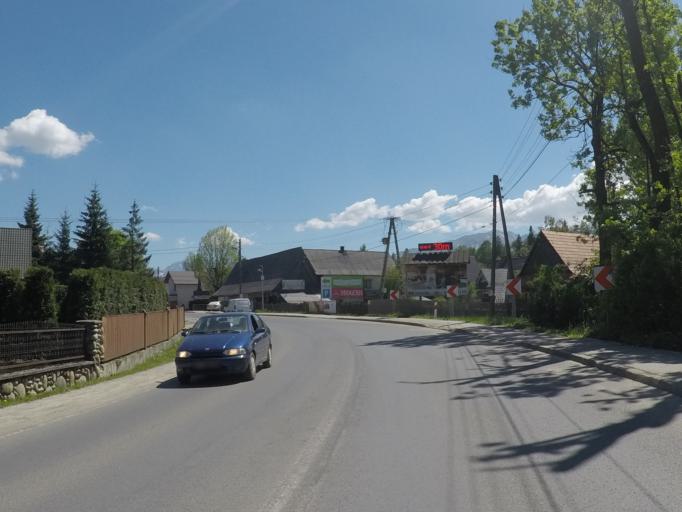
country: PL
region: Lesser Poland Voivodeship
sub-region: Powiat tatrzanski
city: Poronin
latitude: 49.3353
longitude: 20.0070
